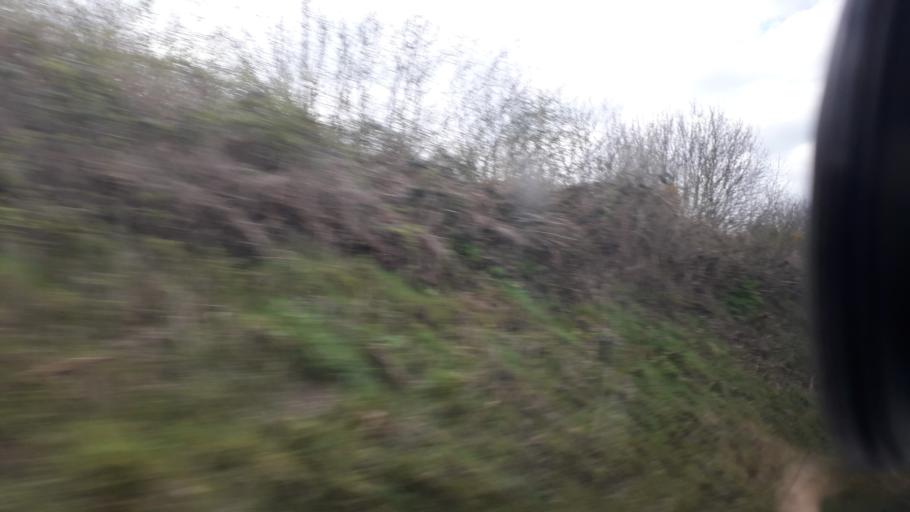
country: IE
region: Leinster
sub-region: An Iarmhi
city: An Muileann gCearr
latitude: 53.6104
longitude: -7.4056
